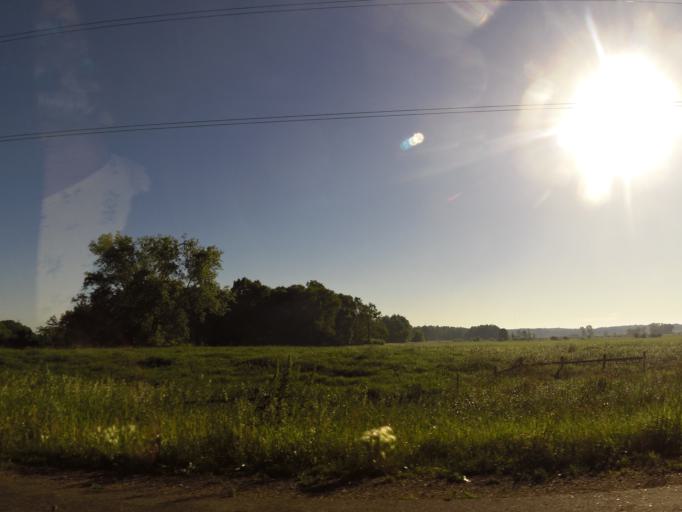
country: US
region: Minnesota
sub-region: Stearns County
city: Waite Park
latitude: 45.5042
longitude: -94.2703
